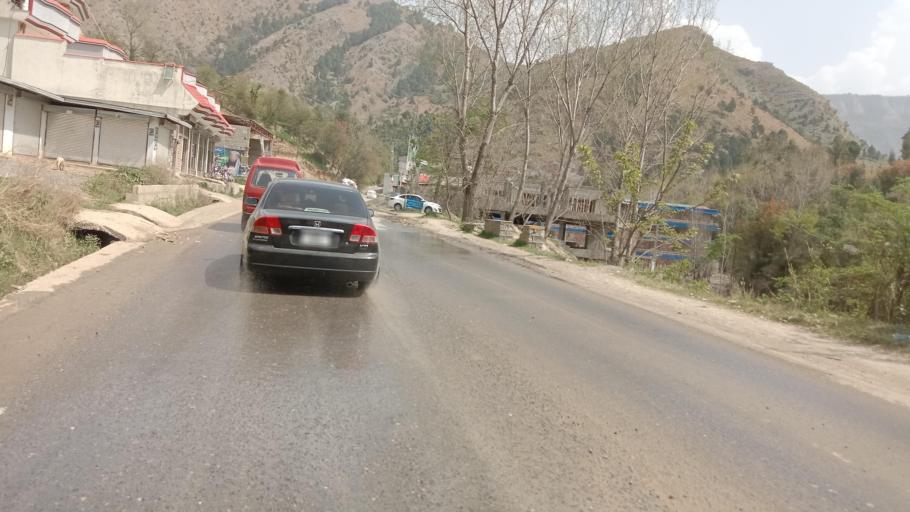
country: PK
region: Khyber Pakhtunkhwa
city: Abbottabad
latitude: 34.1448
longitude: 73.2668
